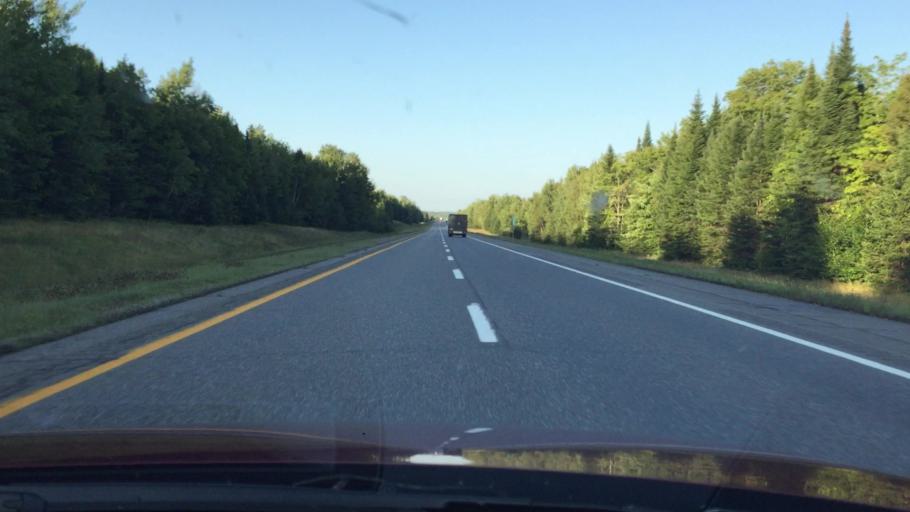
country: US
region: Maine
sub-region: Aroostook County
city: Hodgdon
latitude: 46.1277
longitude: -68.0988
